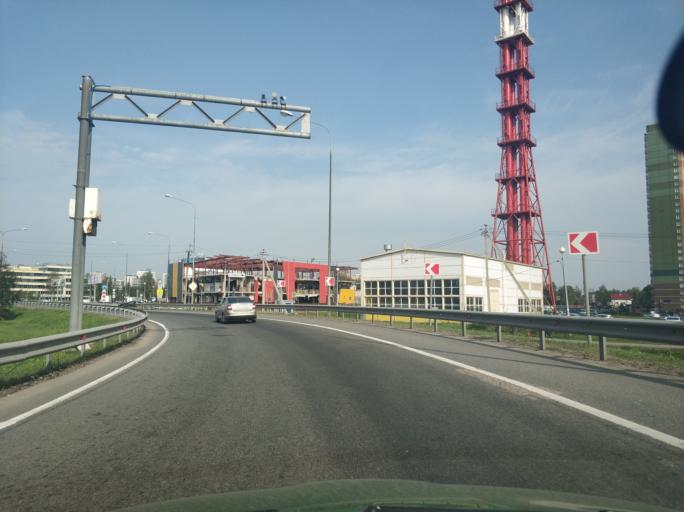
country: RU
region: Leningrad
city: Murino
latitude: 60.0399
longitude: 30.4449
